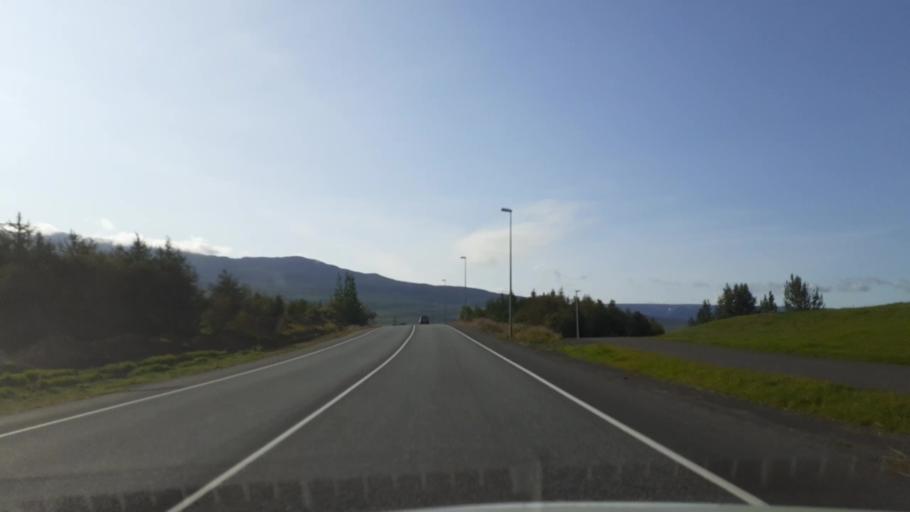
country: IS
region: Northeast
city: Akureyri
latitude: 65.6702
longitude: -18.1107
